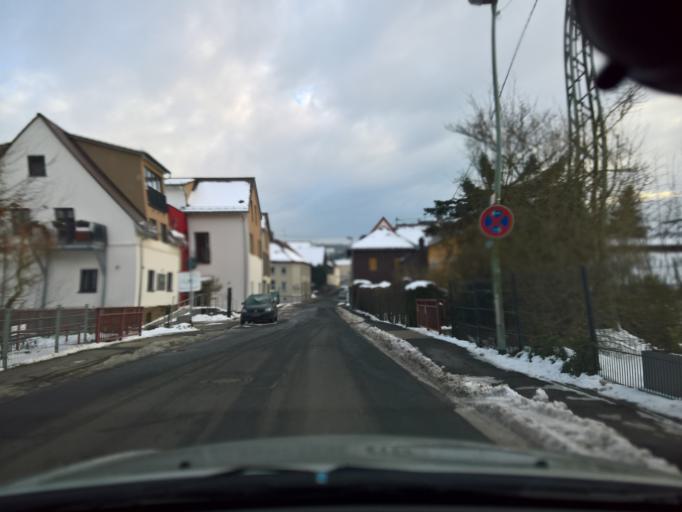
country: DE
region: Hesse
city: Taunusstein
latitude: 50.1553
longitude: 8.1838
